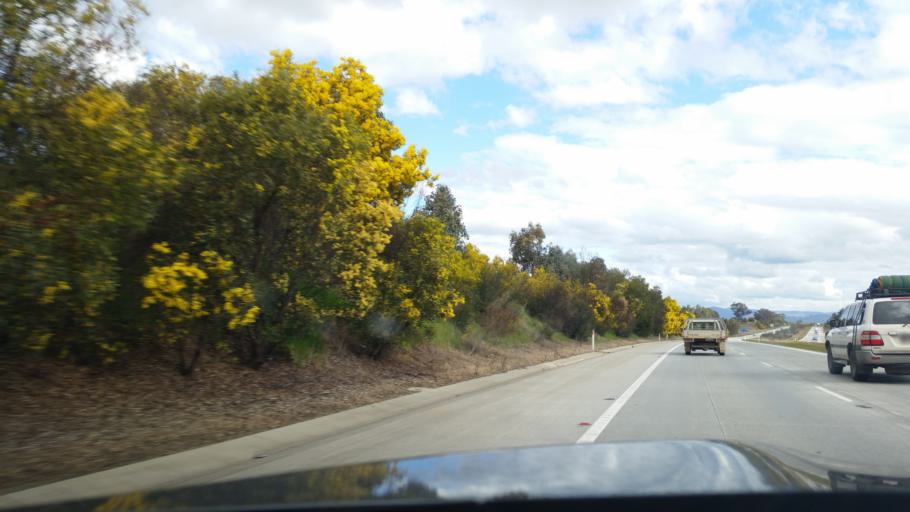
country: AU
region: New South Wales
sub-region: Albury Municipality
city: Lavington
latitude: -36.0018
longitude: 146.9920
